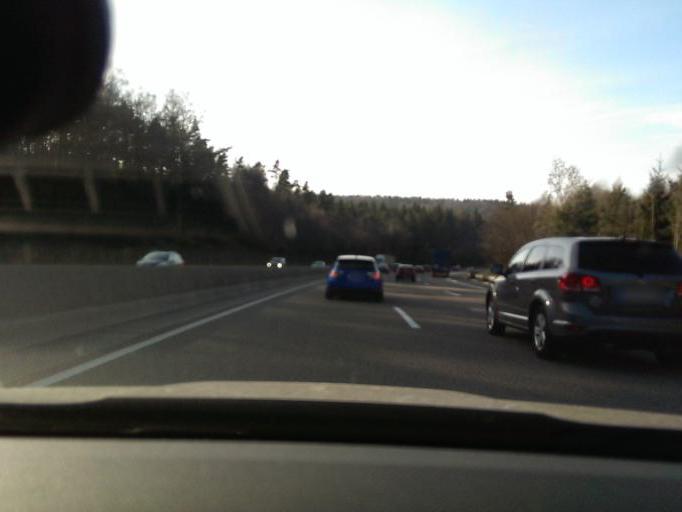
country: DE
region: Hesse
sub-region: Regierungsbezirk Kassel
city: Kirchheim
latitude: 50.8876
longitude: 9.5832
